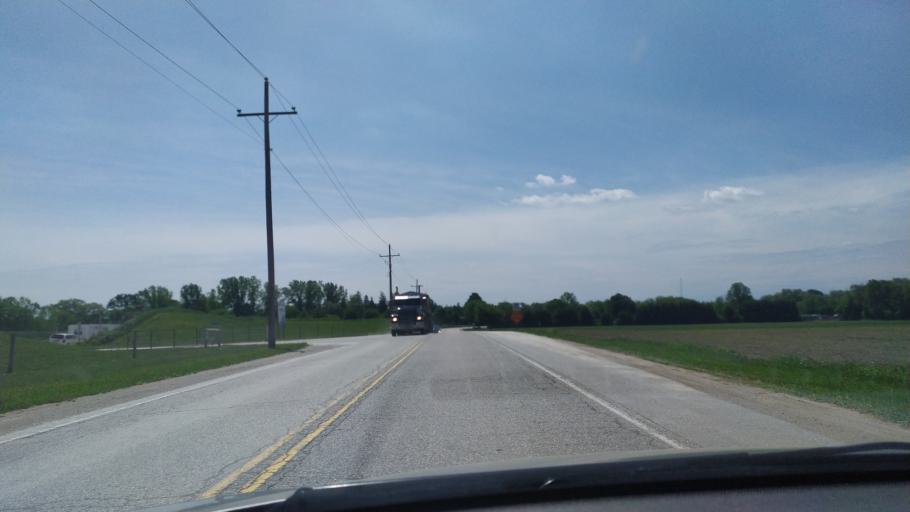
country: CA
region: Ontario
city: Ingersoll
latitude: 42.9954
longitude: -80.9558
